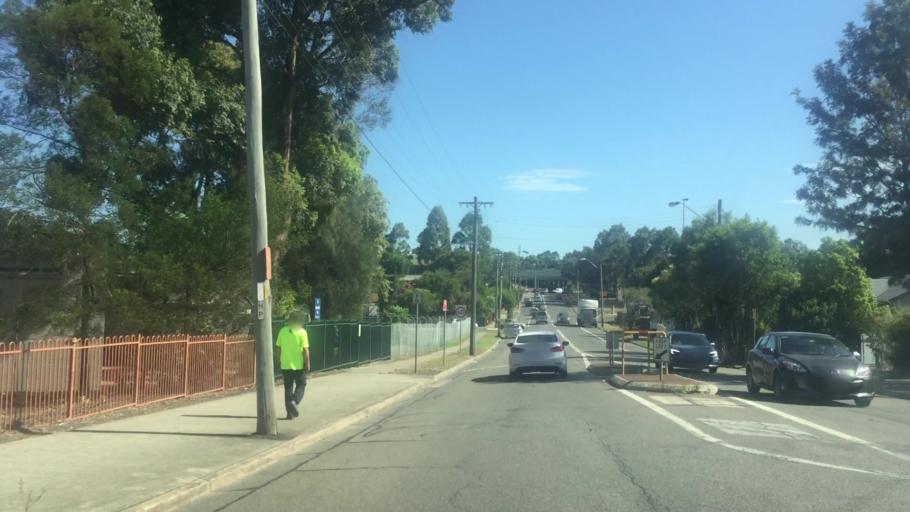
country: AU
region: New South Wales
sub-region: Parramatta
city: City of Parramatta
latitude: -33.8213
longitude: 150.9901
